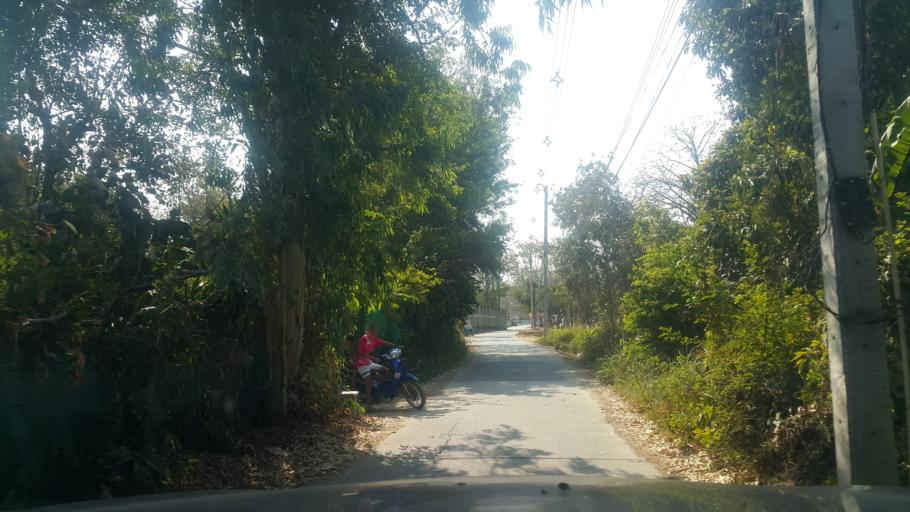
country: TH
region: Nakhon Ratchasima
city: Nakhon Ratchasima
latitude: 14.9323
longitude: 102.0519
